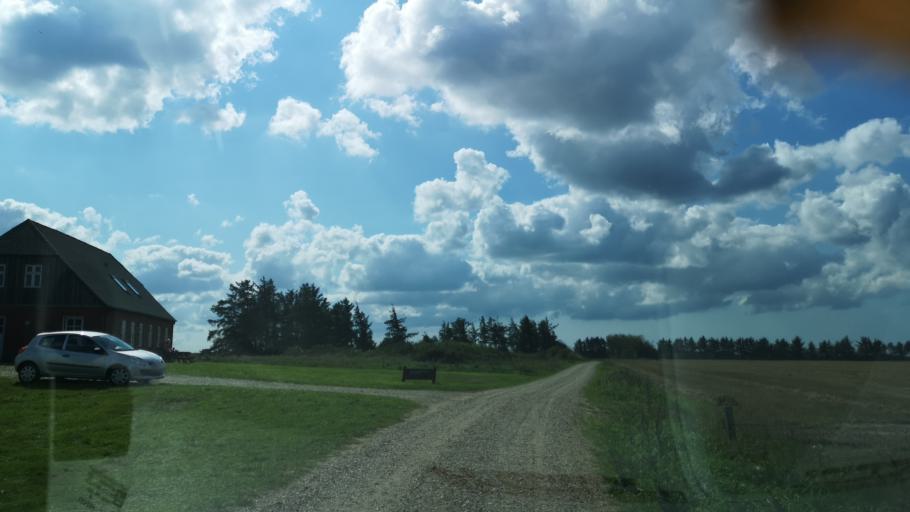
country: DK
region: Central Jutland
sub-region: Ringkobing-Skjern Kommune
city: Skjern
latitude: 55.9059
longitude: 8.3985
